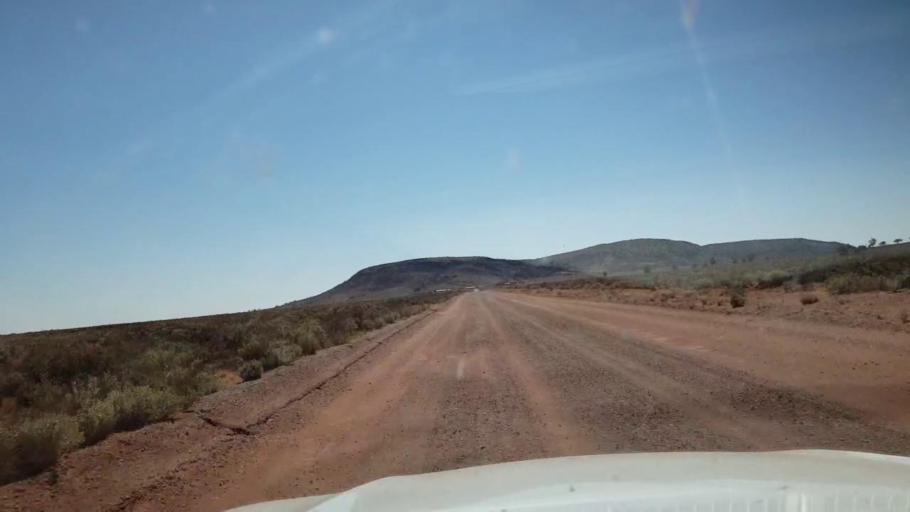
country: AU
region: South Australia
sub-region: Whyalla
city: Whyalla
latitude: -32.7007
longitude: 137.1344
